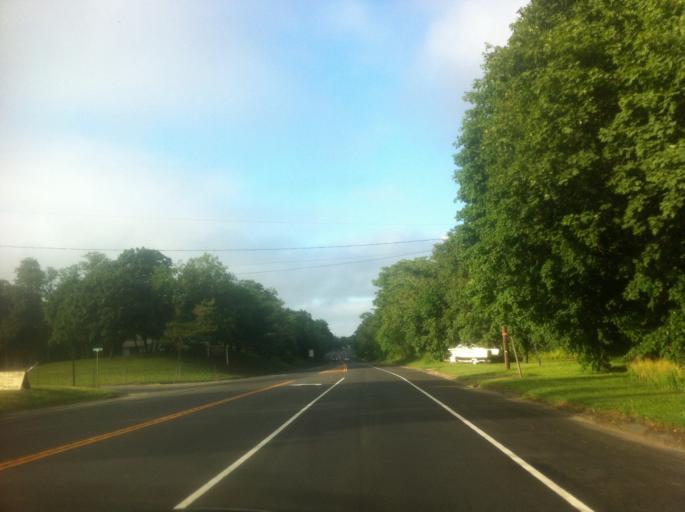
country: US
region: New York
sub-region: Suffolk County
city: Laurel
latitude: 40.9655
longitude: -72.5645
